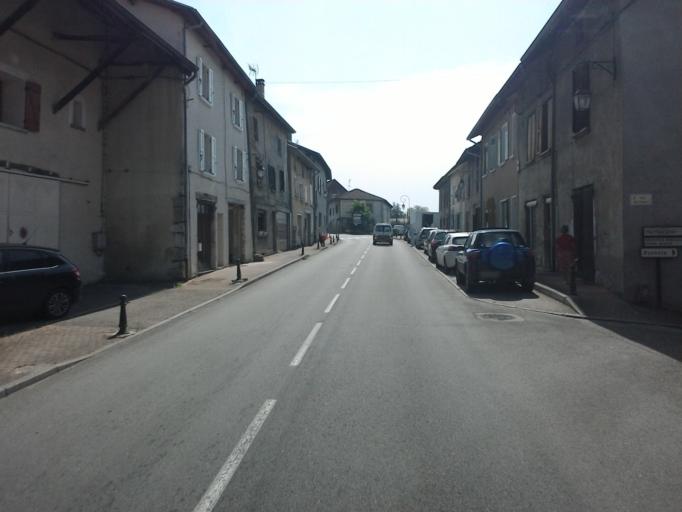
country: FR
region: Rhone-Alpes
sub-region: Departement de l'Isere
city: Montferrat
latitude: 45.4879
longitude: 5.5917
